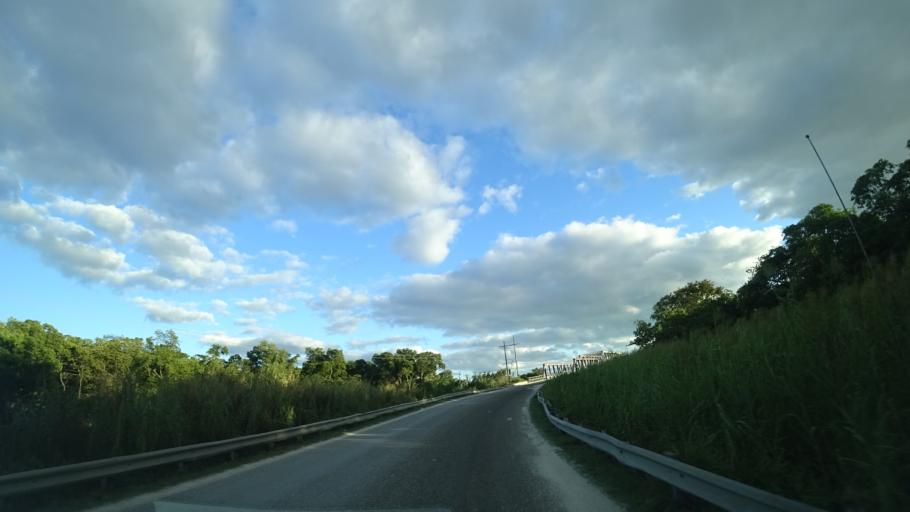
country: BZ
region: Belize
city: Belize City
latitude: 17.5371
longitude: -88.2429
